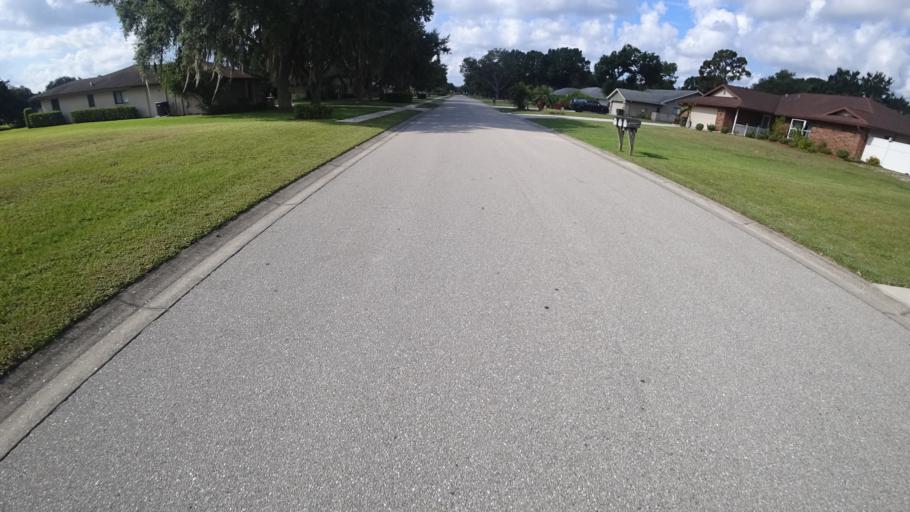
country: US
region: Florida
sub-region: Sarasota County
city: The Meadows
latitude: 27.4307
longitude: -82.4426
